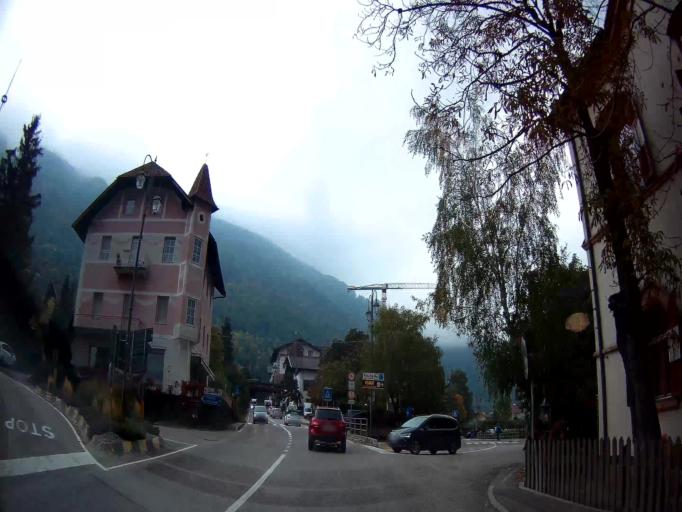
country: IT
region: Trentino-Alto Adige
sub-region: Bolzano
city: Lagundo
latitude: 46.6781
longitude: 11.1195
